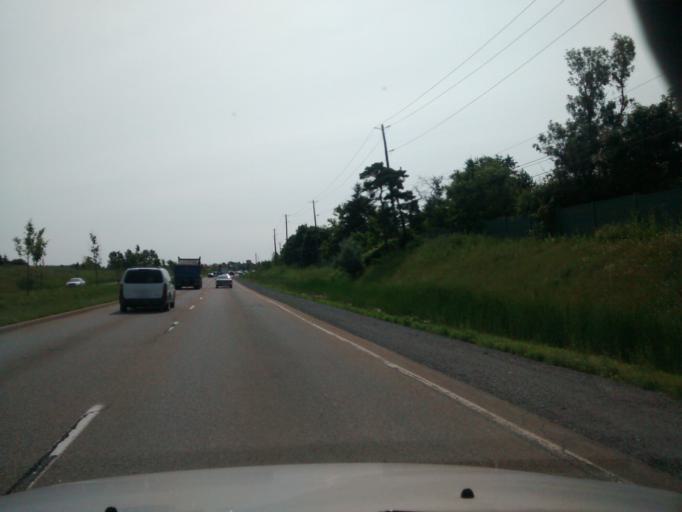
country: CA
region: Ontario
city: Hamilton
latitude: 43.1964
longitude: -79.8014
